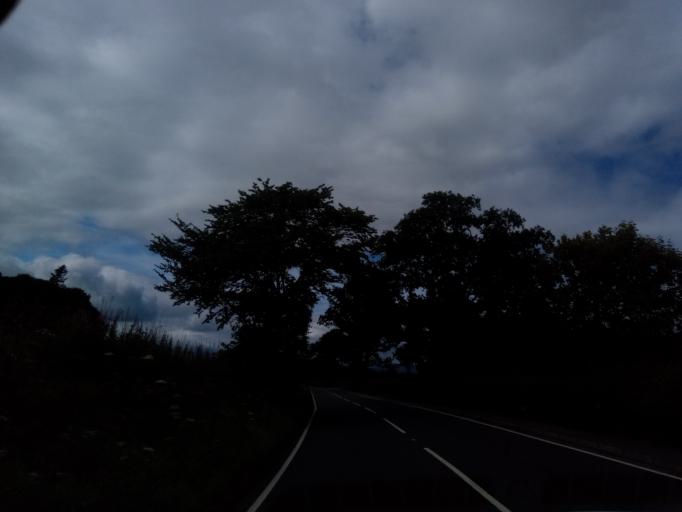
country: GB
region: Scotland
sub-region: Stirling
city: Doune
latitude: 56.1876
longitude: -4.0286
